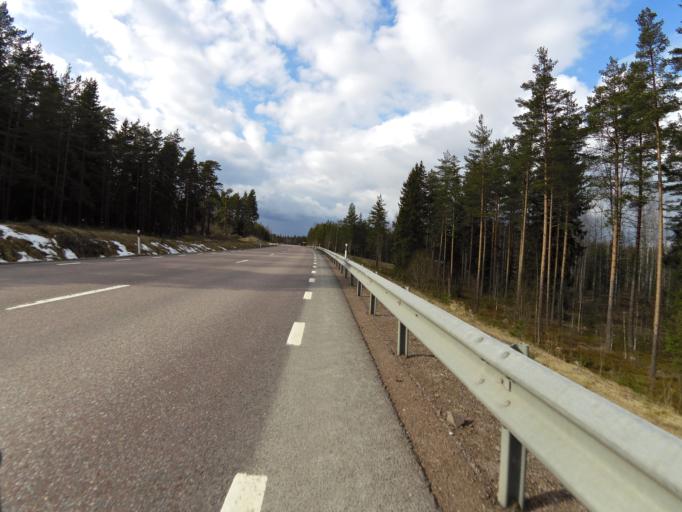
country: SE
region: Gaevleborg
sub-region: Hofors Kommun
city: Hofors
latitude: 60.4916
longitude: 16.4406
